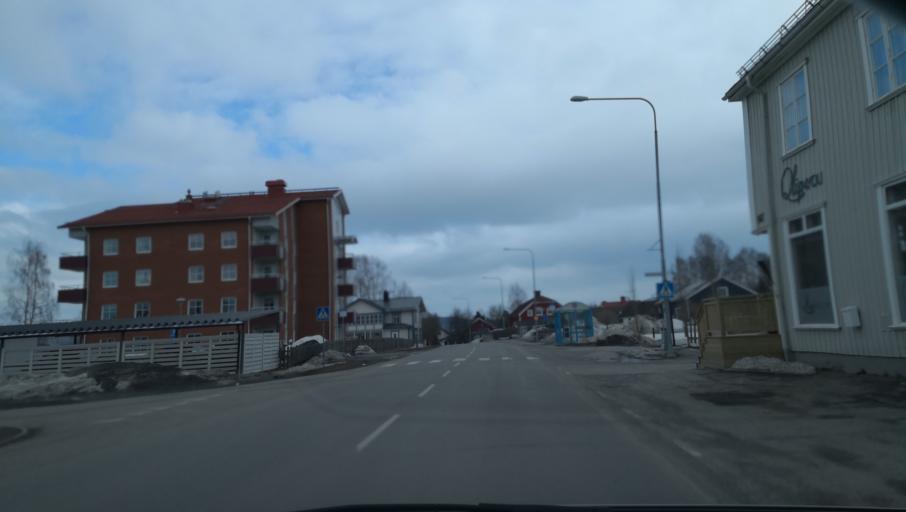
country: SE
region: Vaesterbotten
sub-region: Vannas Kommun
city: Vannasby
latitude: 63.9125
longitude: 19.8215
